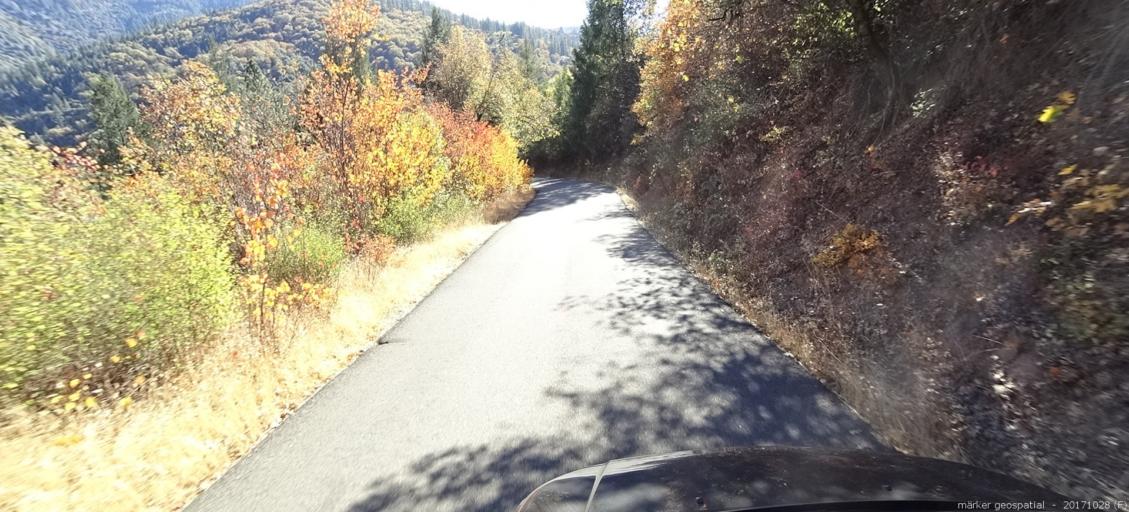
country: US
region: California
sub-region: Trinity County
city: Lewiston
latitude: 40.7980
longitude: -122.6116
